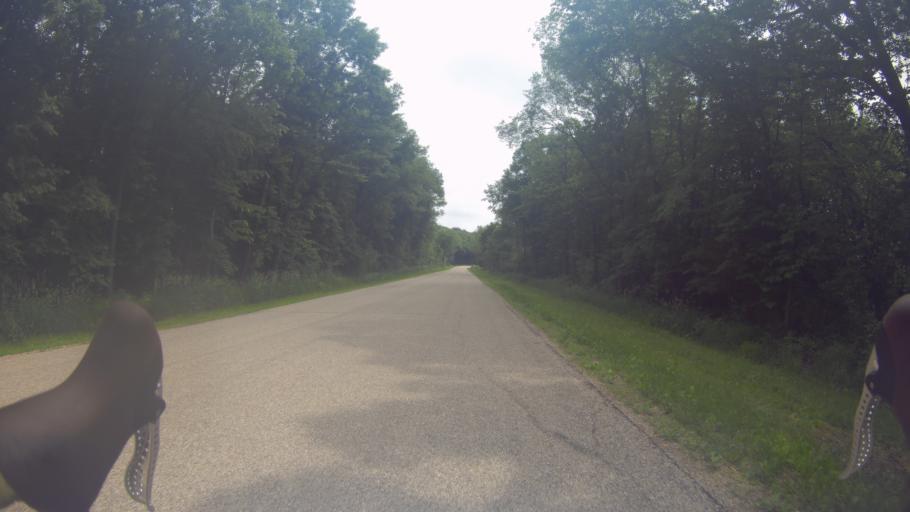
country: US
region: Wisconsin
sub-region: Jefferson County
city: Cambridge
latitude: 42.9214
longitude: -89.0272
